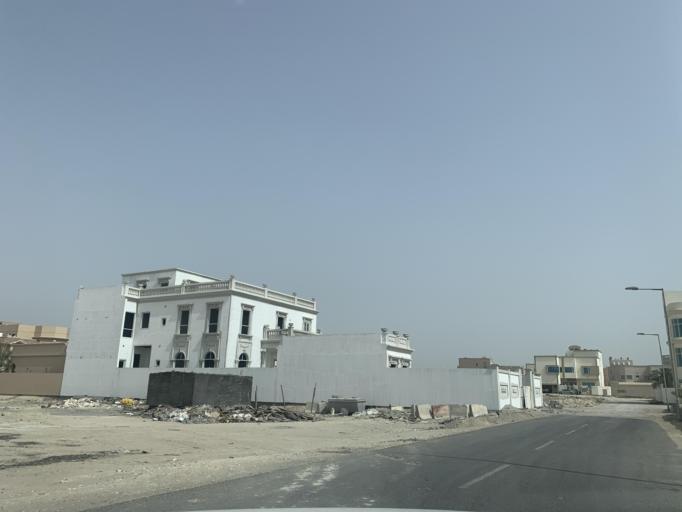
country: BH
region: Northern
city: Madinat `Isa
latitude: 26.1545
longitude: 50.5157
